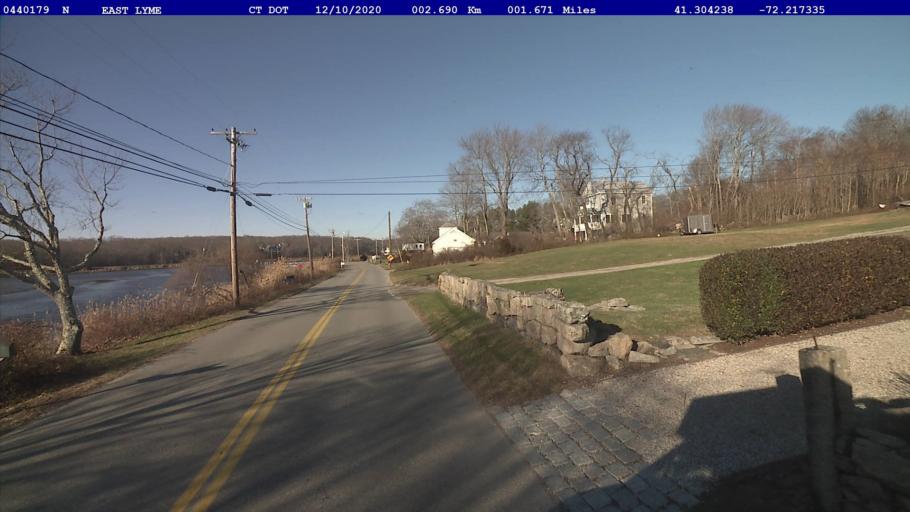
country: US
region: Connecticut
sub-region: New London County
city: Niantic
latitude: 41.3042
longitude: -72.2173
